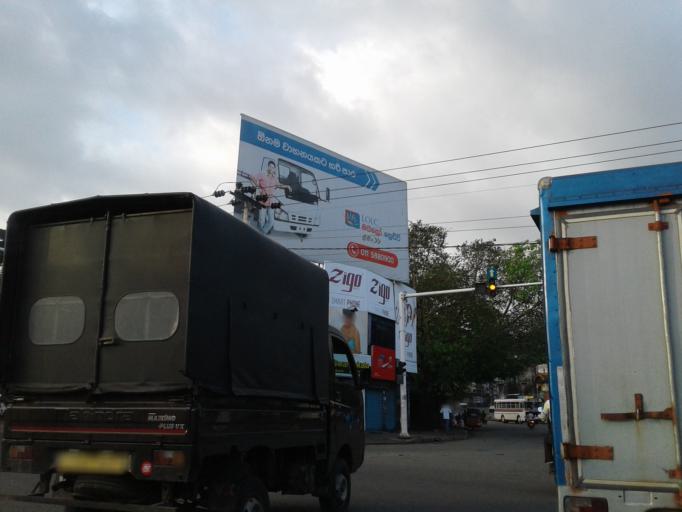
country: LK
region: Western
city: Mulleriyawa
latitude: 6.9357
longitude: 79.9843
